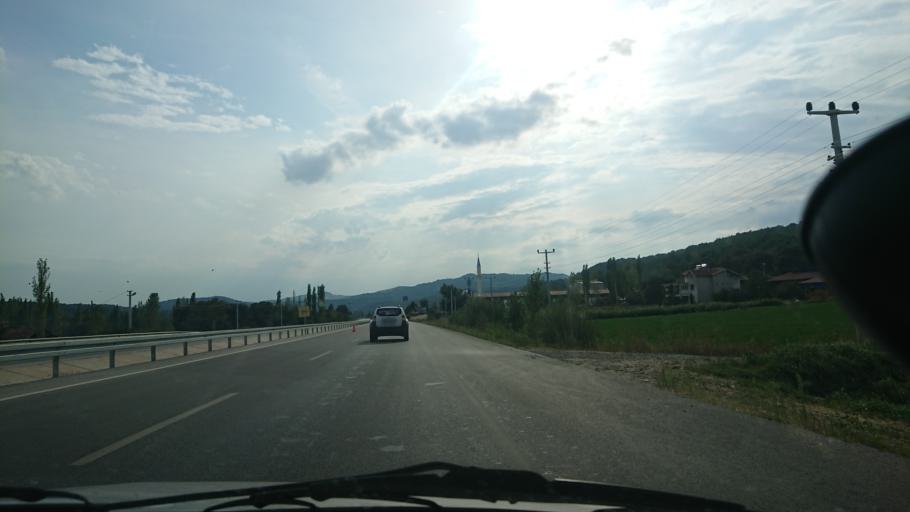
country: TR
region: Kuetahya
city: Gediz
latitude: 38.9393
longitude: 29.3194
